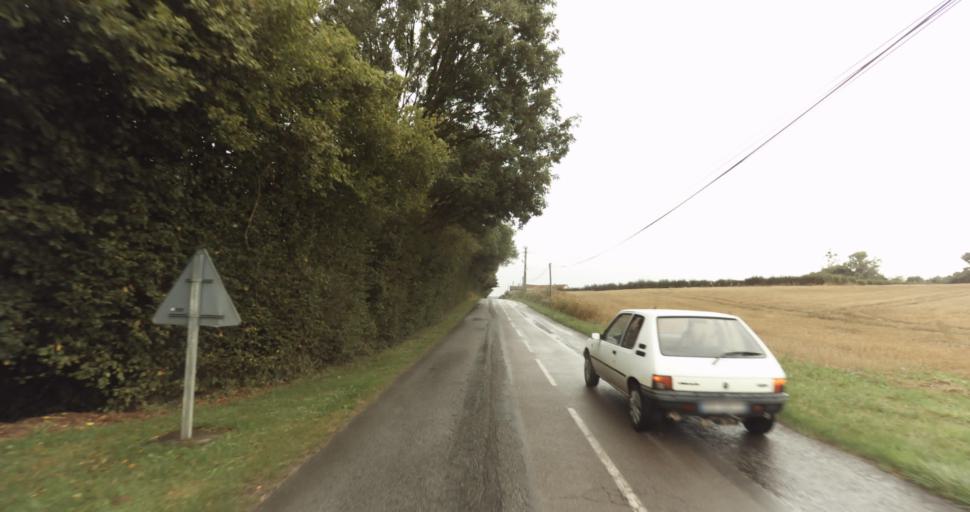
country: FR
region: Lower Normandy
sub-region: Departement de l'Orne
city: Sainte-Gauburge-Sainte-Colombe
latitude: 48.7229
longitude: 0.4304
